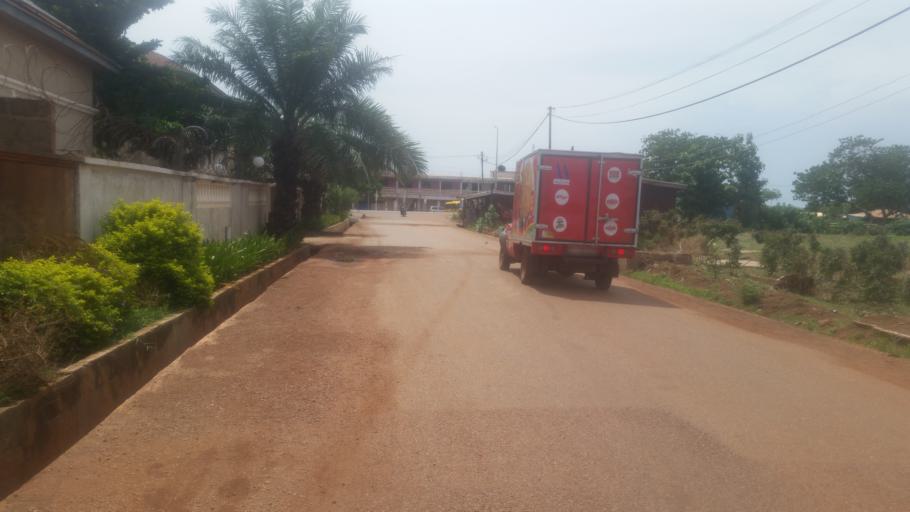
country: GH
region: Northern
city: Tamale
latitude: 9.4430
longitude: -0.8449
